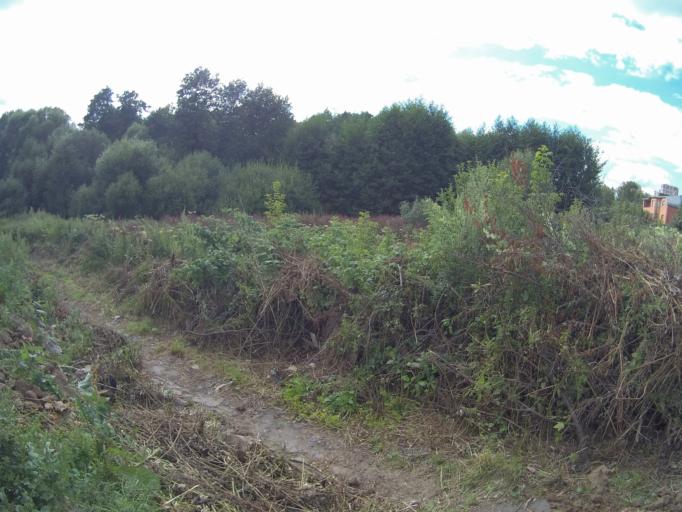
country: RU
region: Vladimir
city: Vladimir
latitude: 56.1153
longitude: 40.3846
